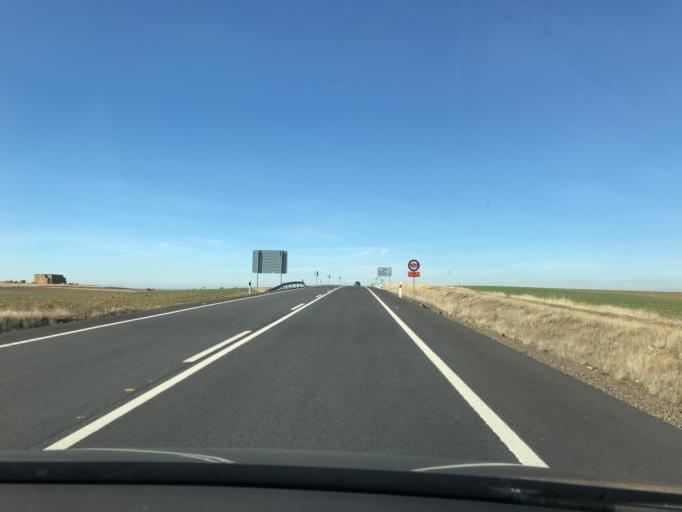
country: ES
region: Extremadura
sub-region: Provincia de Badajoz
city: Granja de Torrehermosa
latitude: 38.2983
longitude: -5.5599
